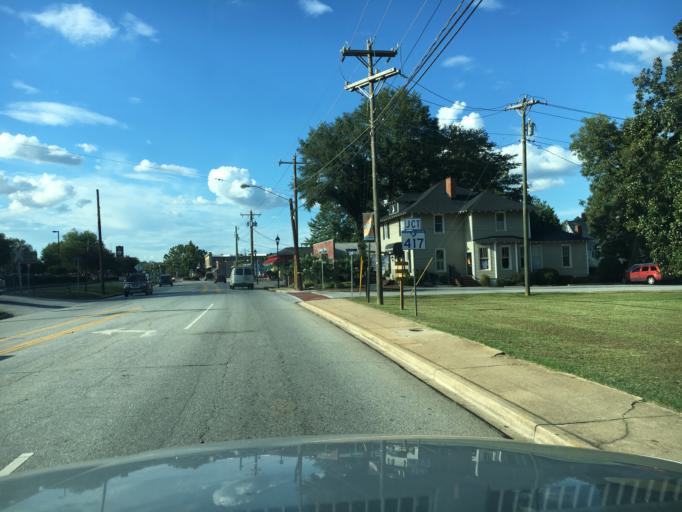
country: US
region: South Carolina
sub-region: Greenville County
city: Simpsonville
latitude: 34.7354
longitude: -82.2546
